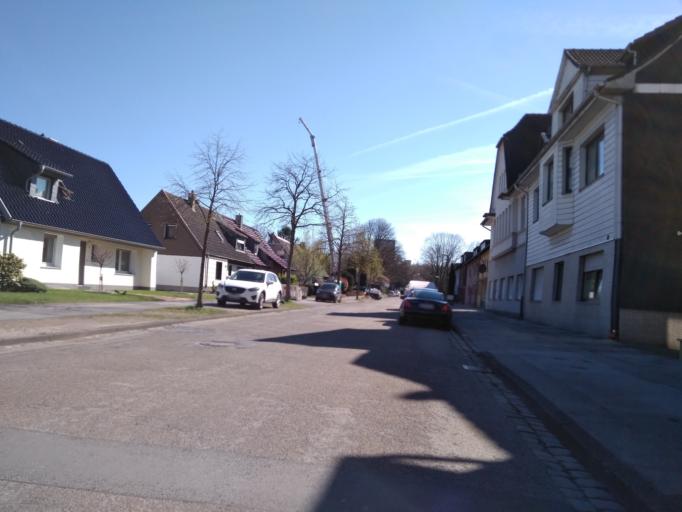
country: DE
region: North Rhine-Westphalia
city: Marl
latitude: 51.6081
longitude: 7.0736
